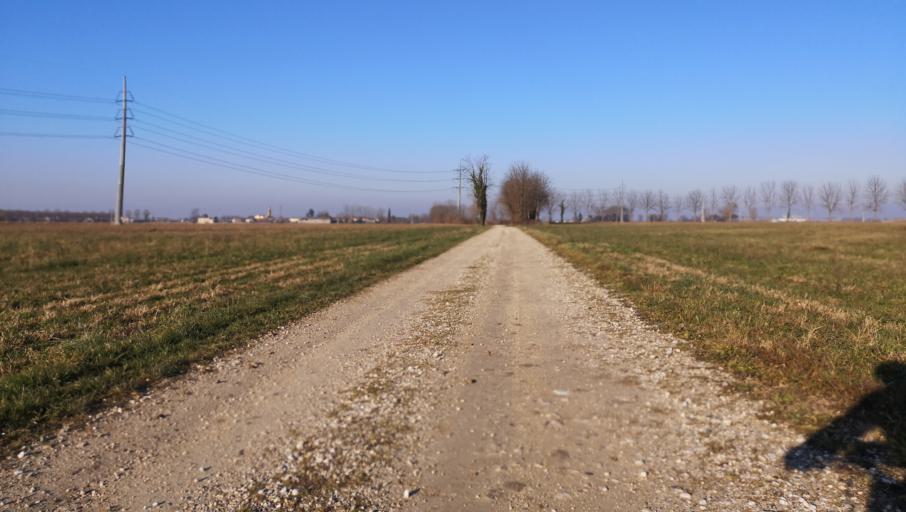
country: IT
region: Friuli Venezia Giulia
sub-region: Provincia di Udine
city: Santa Maria la Longa
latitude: 45.9525
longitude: 13.2983
